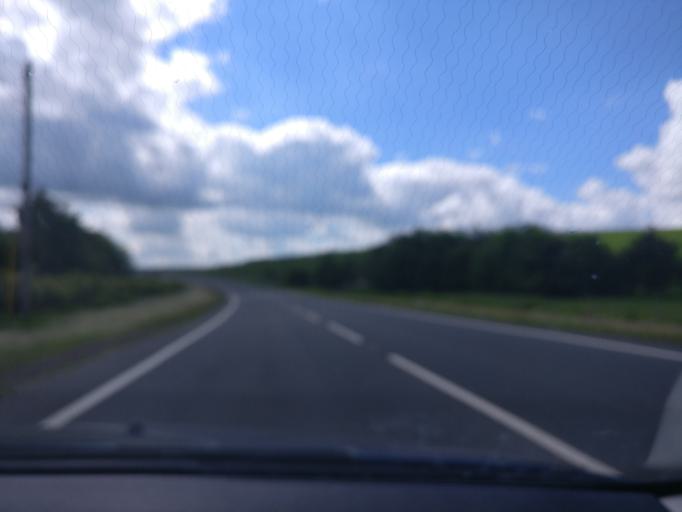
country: GB
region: Scotland
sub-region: Fife
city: Pathhead
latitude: 55.7917
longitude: -2.9642
